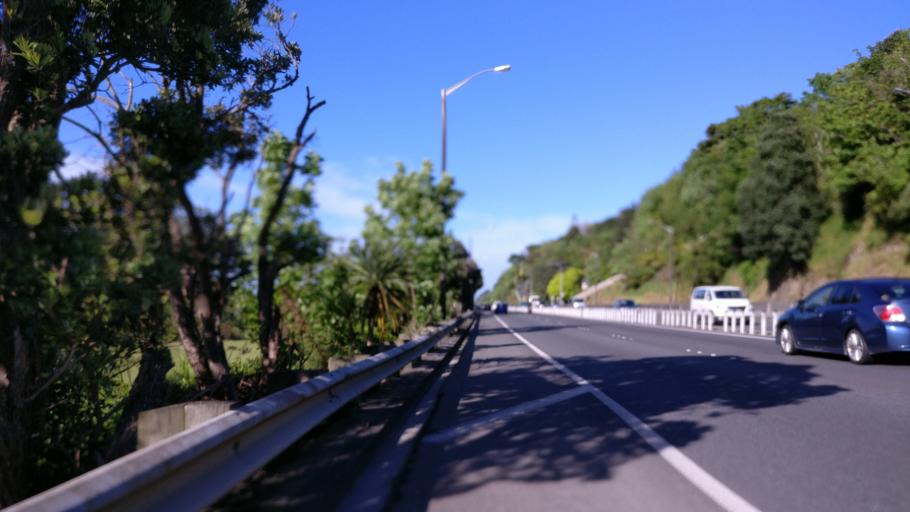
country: NZ
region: Wellington
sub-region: Lower Hutt City
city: Lower Hutt
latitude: -41.1966
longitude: 174.9179
